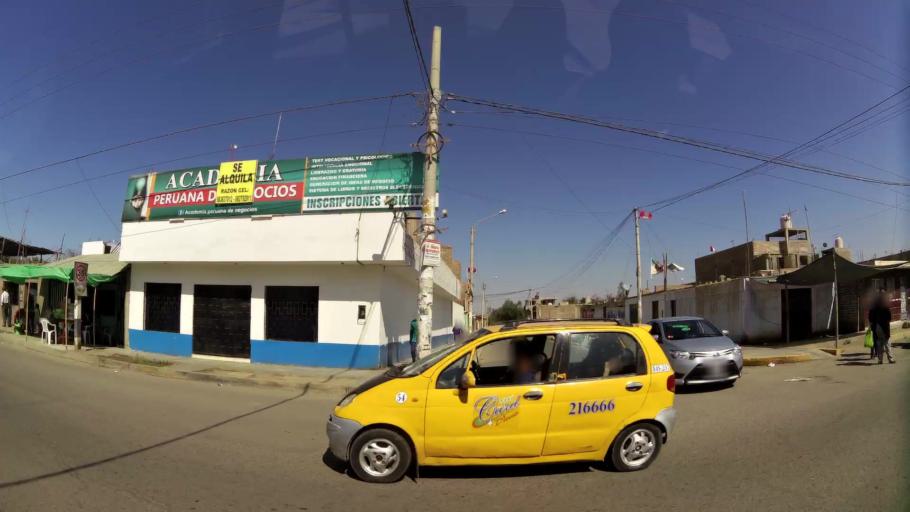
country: PE
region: Ica
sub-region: Provincia de Ica
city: La Tinguina
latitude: -14.0449
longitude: -75.7080
